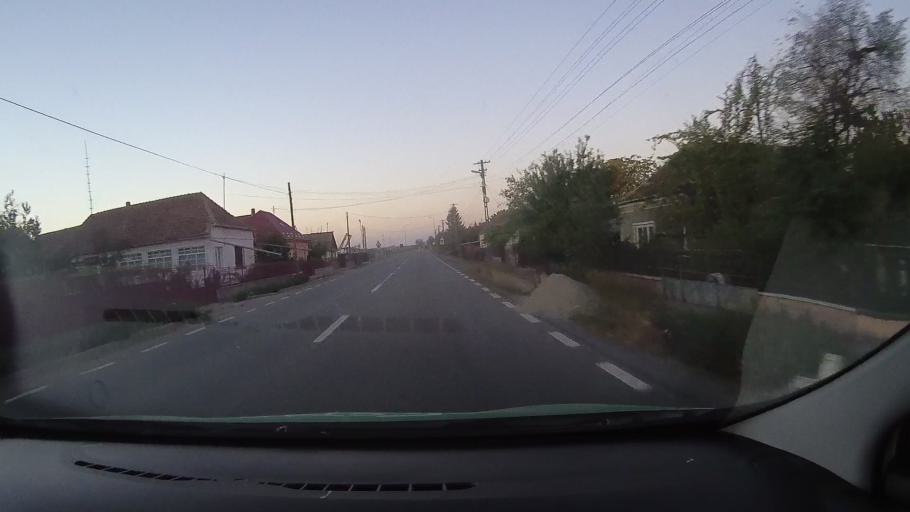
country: RO
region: Bihor
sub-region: Comuna Tarcea
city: Tarcea
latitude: 47.4656
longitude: 22.1664
